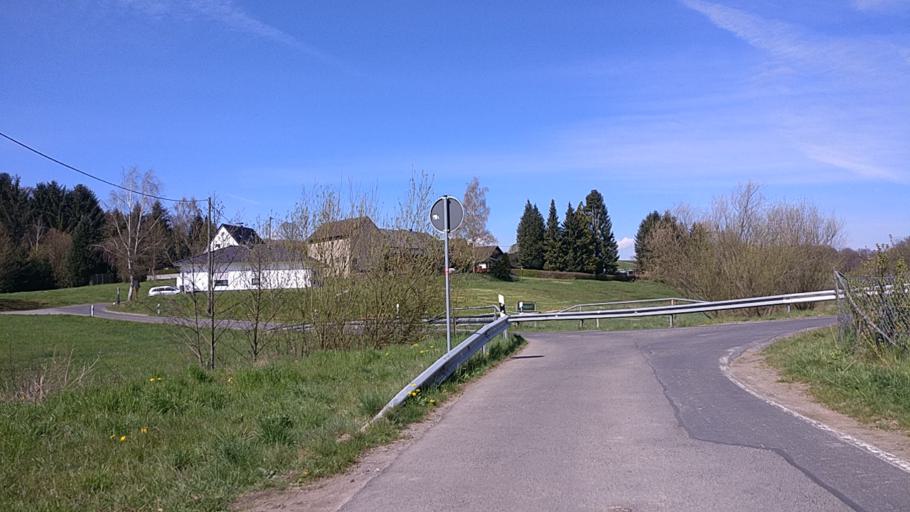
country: DE
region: Rheinland-Pfalz
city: Asbach
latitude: 50.6433
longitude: 7.4358
